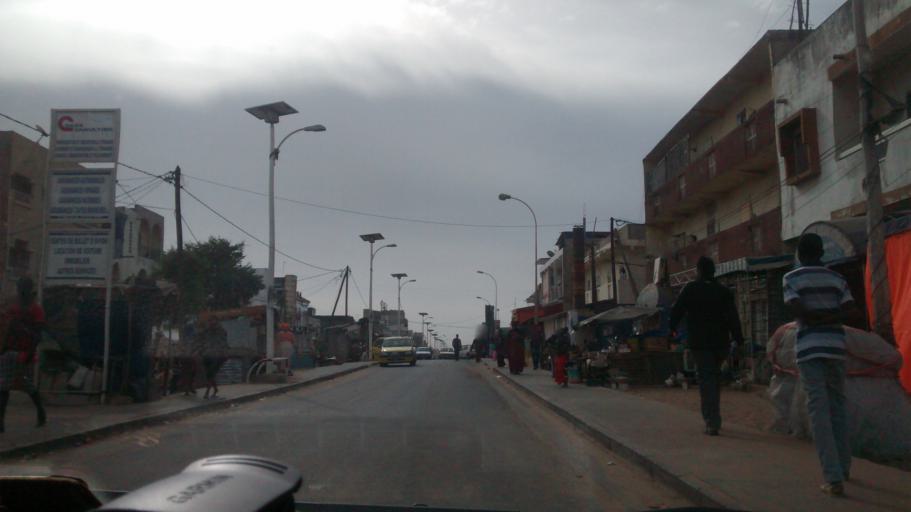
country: SN
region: Dakar
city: Pikine
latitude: 14.7817
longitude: -17.3814
